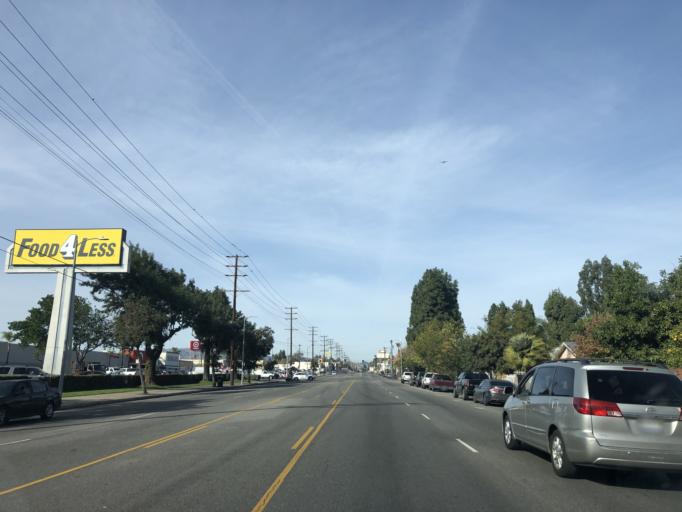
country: US
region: California
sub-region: Los Angeles County
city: San Fernando
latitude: 34.2447
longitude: -118.4172
